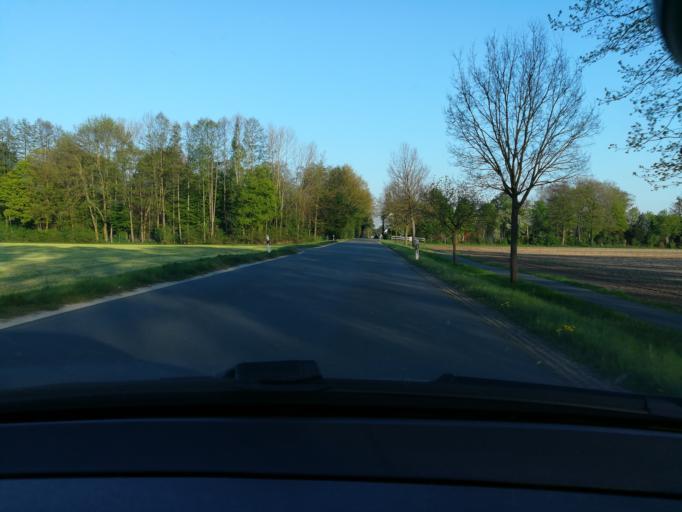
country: DE
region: North Rhine-Westphalia
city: Versmold
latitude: 52.0610
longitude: 8.1751
